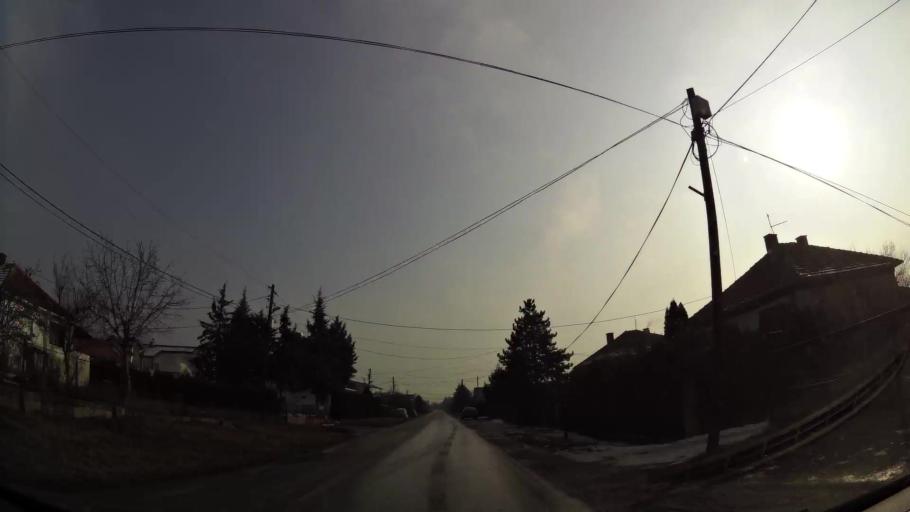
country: MK
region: Ilinden
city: Marino
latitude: 41.9900
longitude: 21.5910
